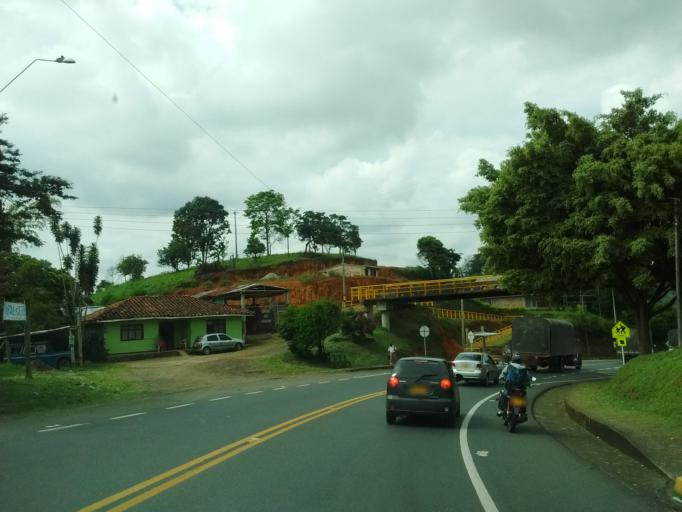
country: CO
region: Cauca
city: Caldono
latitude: 2.7996
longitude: -76.5513
